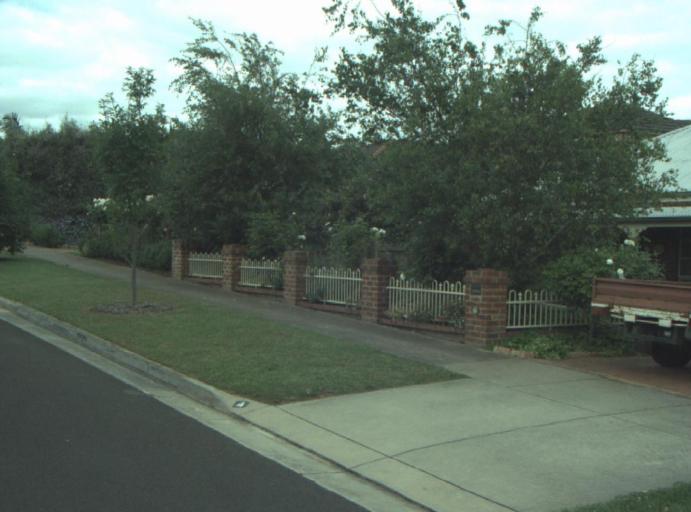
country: AU
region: Victoria
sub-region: Greater Geelong
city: Wandana Heights
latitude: -38.2043
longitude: 144.3160
